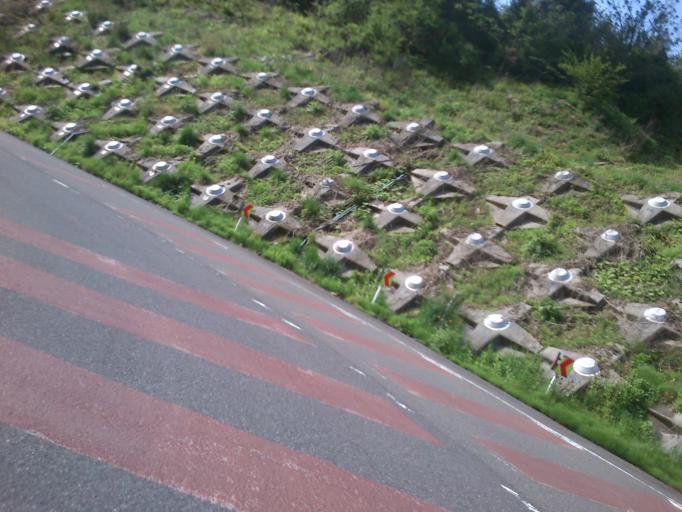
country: JP
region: Kyoto
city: Miyazu
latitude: 35.6365
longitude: 135.2005
